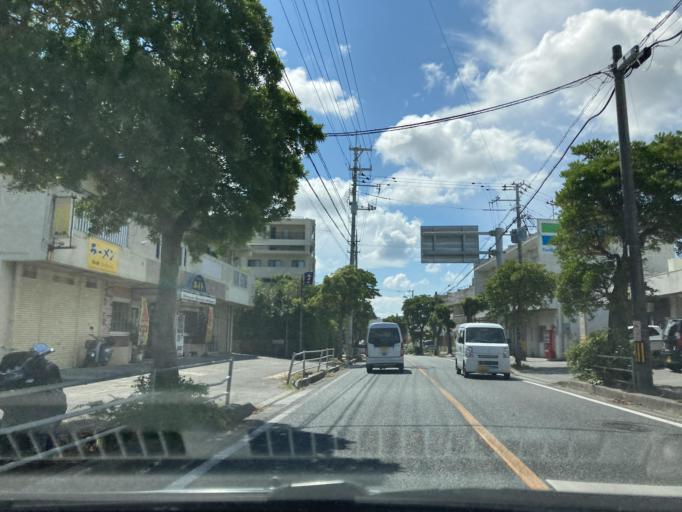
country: JP
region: Okinawa
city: Tomigusuku
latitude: 26.1855
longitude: 127.7115
